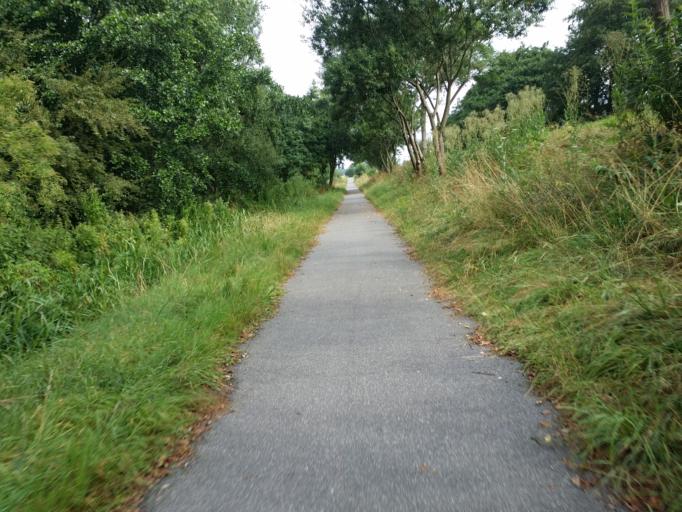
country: DE
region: Schleswig-Holstein
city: Heiligenstedten
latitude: 53.9149
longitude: 9.4887
